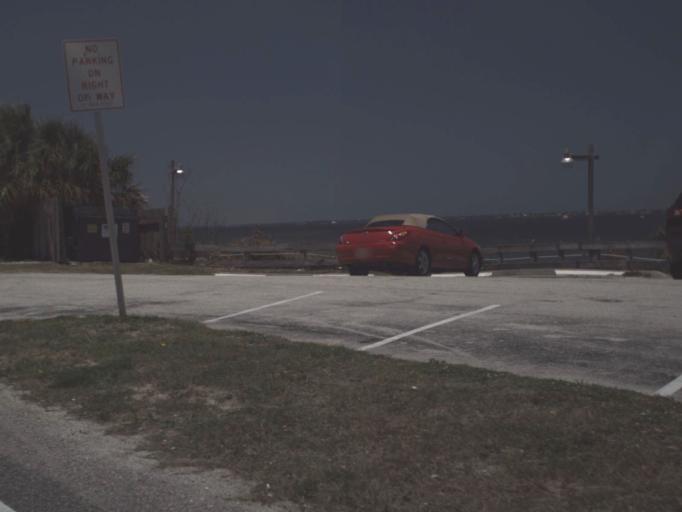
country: US
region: Florida
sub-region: Brevard County
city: Malabar
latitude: 28.0193
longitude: -80.5708
